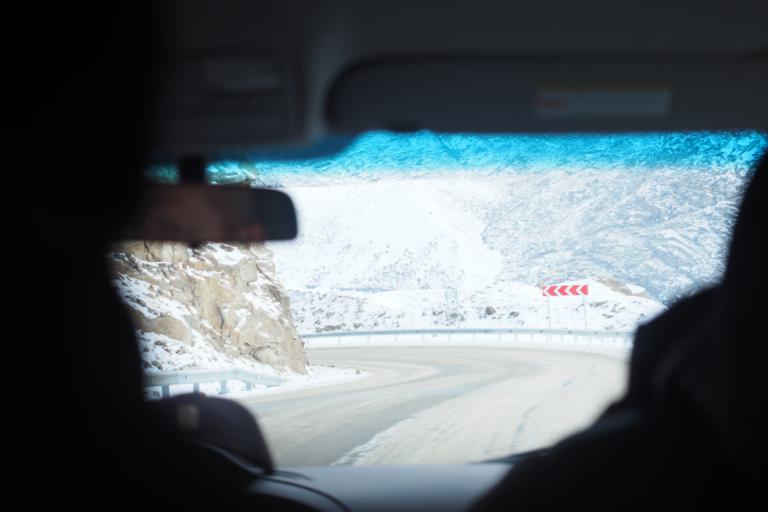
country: RU
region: Altay
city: Inya
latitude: 50.5012
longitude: 86.5636
